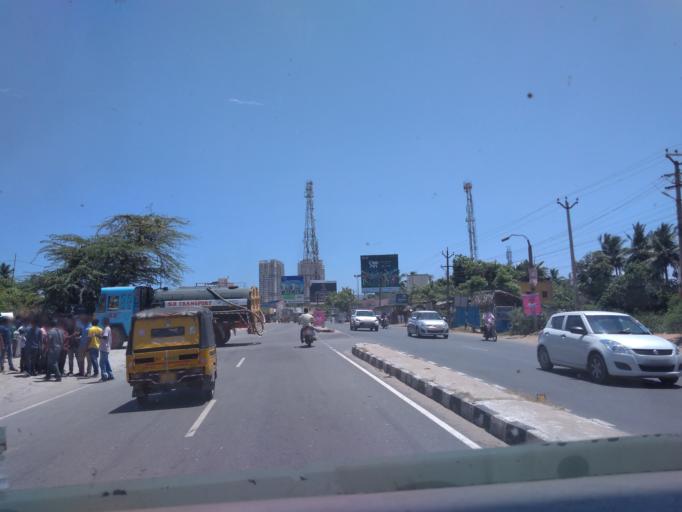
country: IN
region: Tamil Nadu
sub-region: Kancheepuram
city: Injambakkam
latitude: 12.8203
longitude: 80.2305
